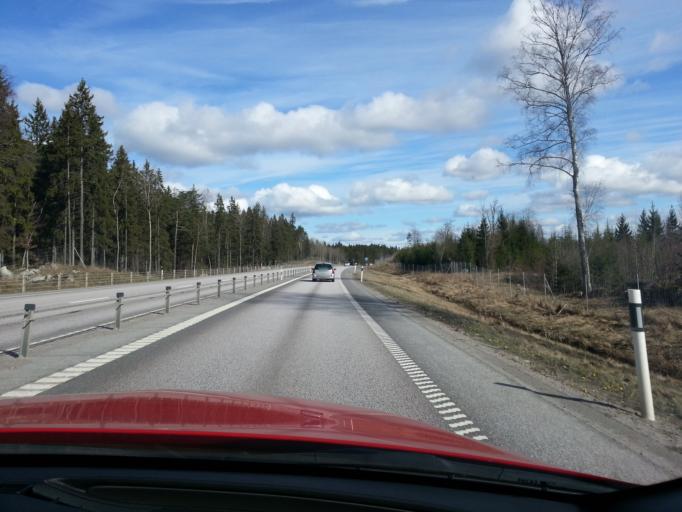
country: SE
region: Uppsala
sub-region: Uppsala Kommun
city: Storvreta
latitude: 59.9224
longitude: 17.7653
